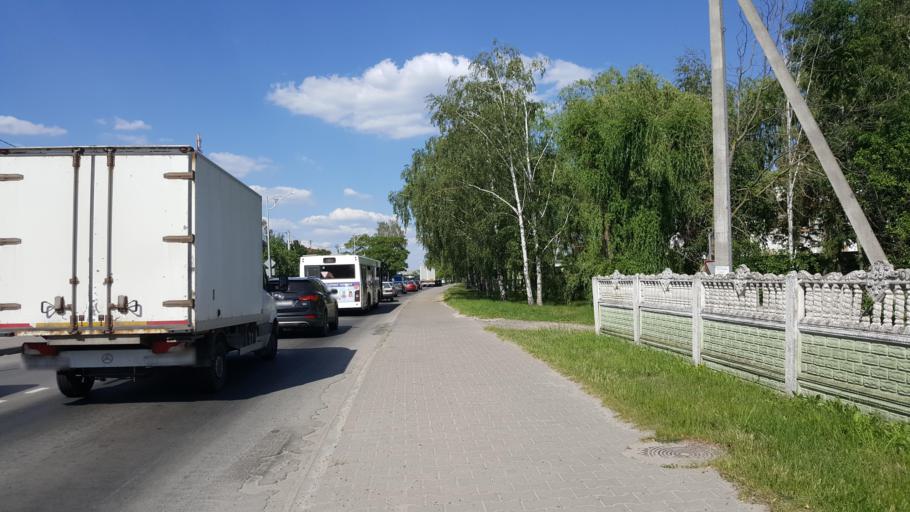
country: BY
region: Brest
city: Horad Kobryn
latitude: 52.2200
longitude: 24.3624
